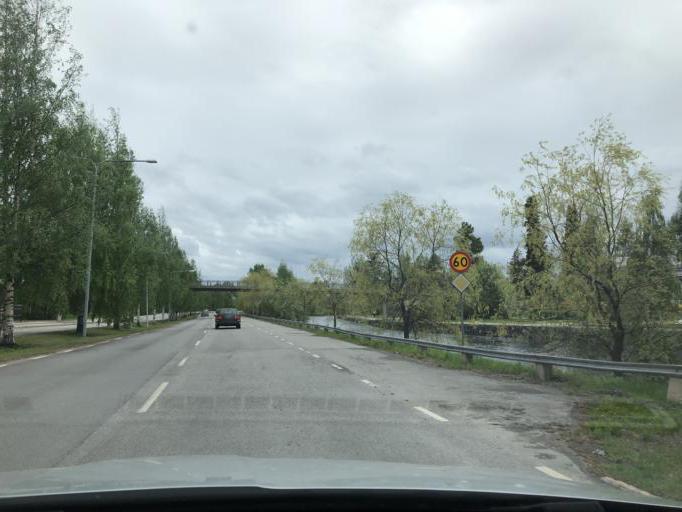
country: SE
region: Norrbotten
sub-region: Pitea Kommun
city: Pitea
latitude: 65.3148
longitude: 21.4920
